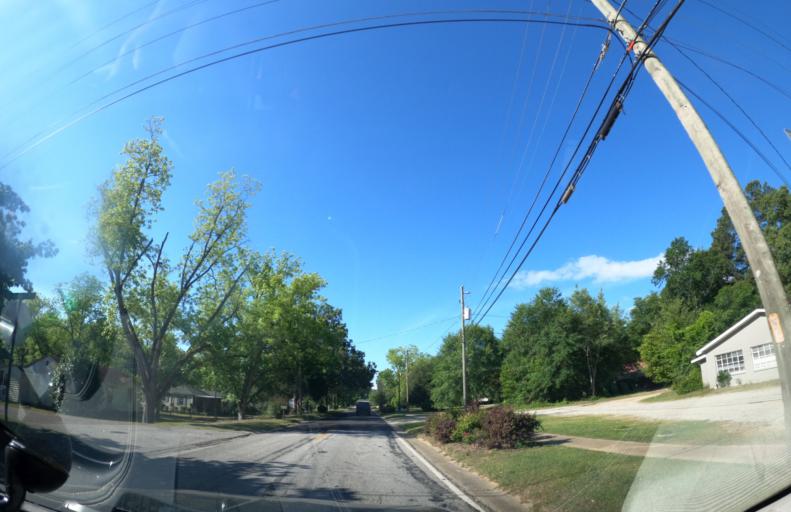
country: US
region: Georgia
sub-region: Columbia County
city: Harlem
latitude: 33.4092
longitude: -82.3141
